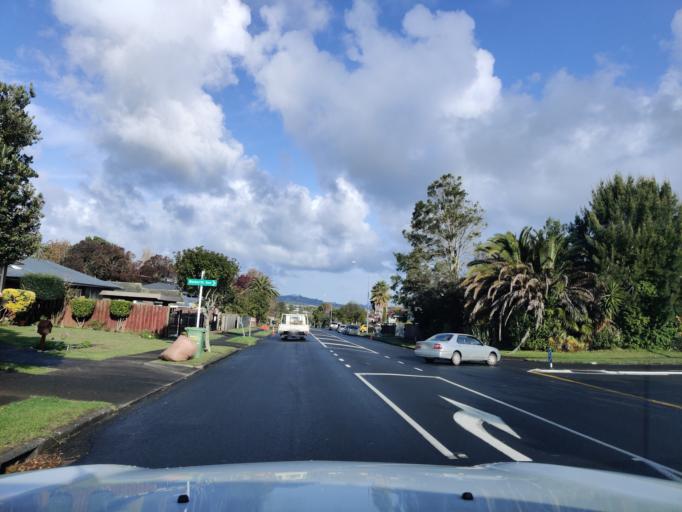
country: NZ
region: Auckland
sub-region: Auckland
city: Pakuranga
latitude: -36.9059
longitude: 174.8962
